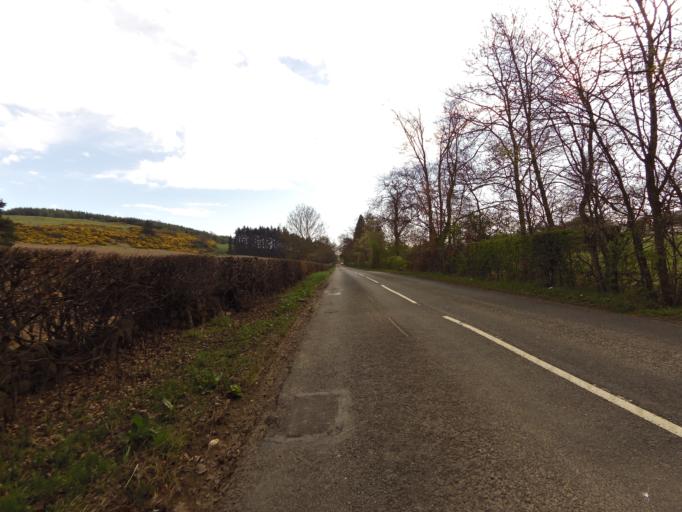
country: GB
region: Scotland
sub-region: Fife
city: Newburgh
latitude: 56.3241
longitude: -3.2298
